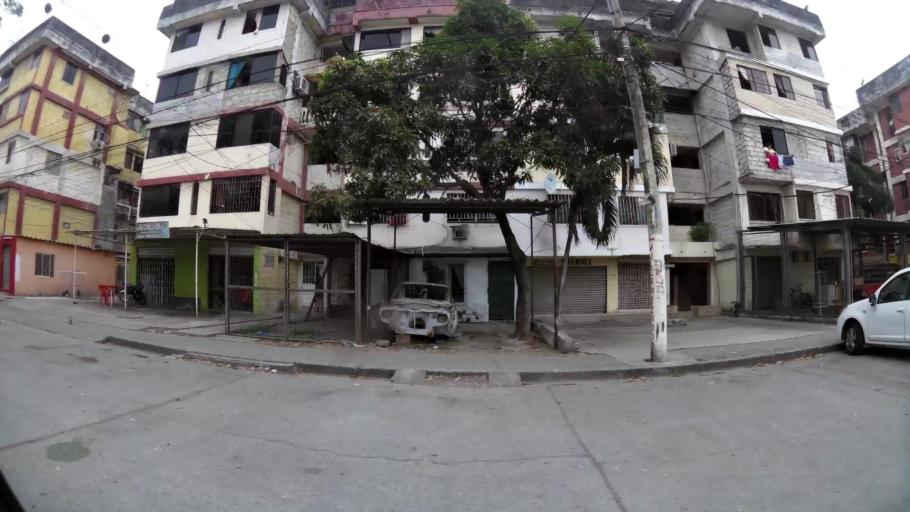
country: EC
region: Guayas
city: Eloy Alfaro
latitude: -2.1252
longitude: -79.8856
